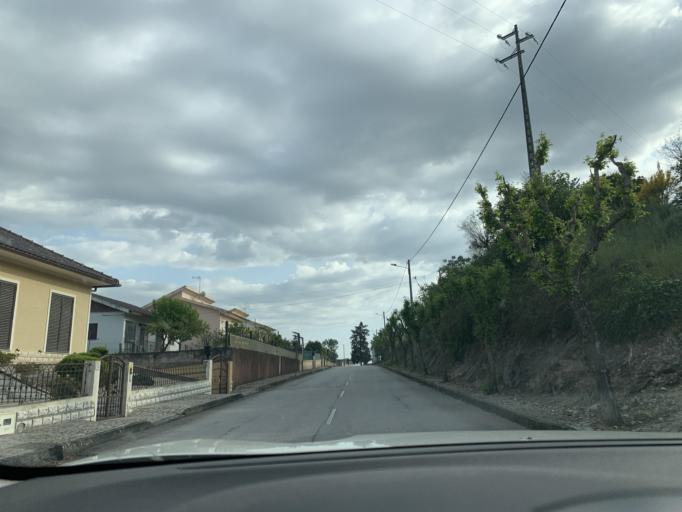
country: PT
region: Guarda
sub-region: Fornos de Algodres
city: Fornos de Algodres
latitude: 40.5773
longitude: -7.6422
